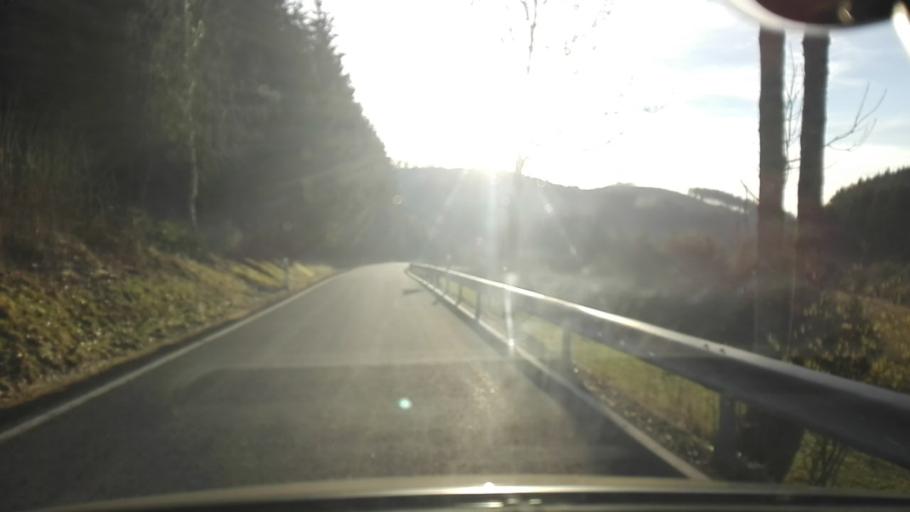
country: DE
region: North Rhine-Westphalia
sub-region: Regierungsbezirk Arnsberg
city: Lennestadt
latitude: 51.1926
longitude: 8.0856
